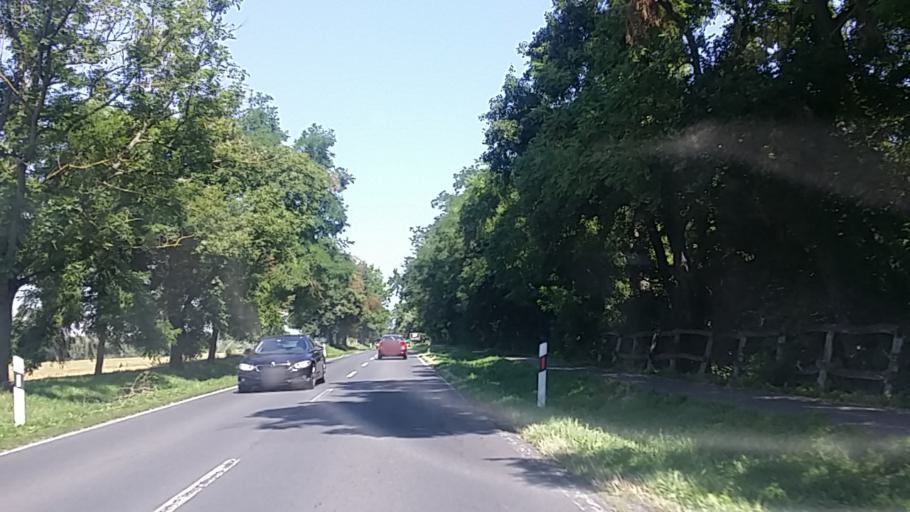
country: HU
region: Zala
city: Keszthely
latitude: 46.7173
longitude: 17.2424
